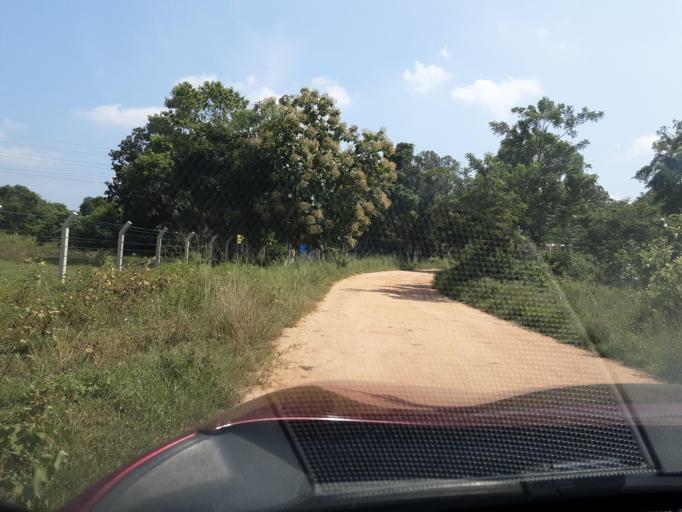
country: LK
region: Central
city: Sigiriya
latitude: 8.0055
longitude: 80.7460
